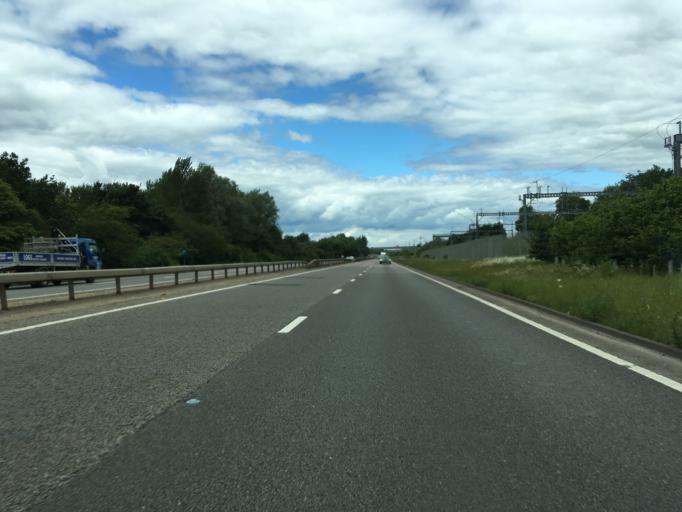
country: GB
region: England
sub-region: Milton Keynes
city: Milton Keynes
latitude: 52.0246
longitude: -0.7630
